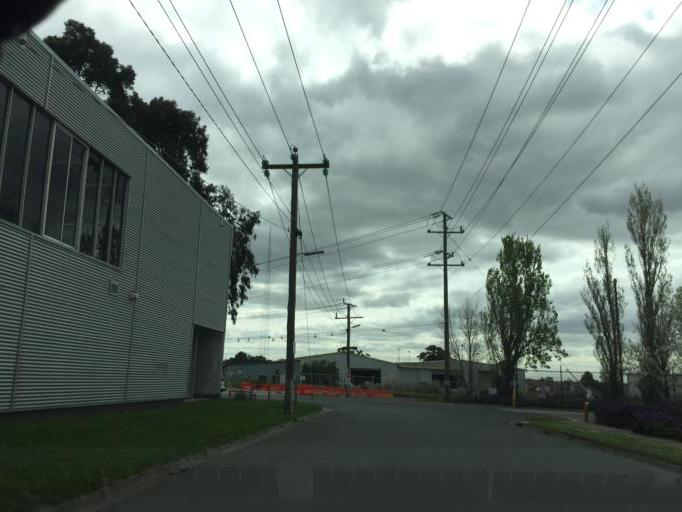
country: AU
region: Victoria
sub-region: Hobsons Bay
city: South Kingsville
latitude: -37.8200
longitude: 144.8602
